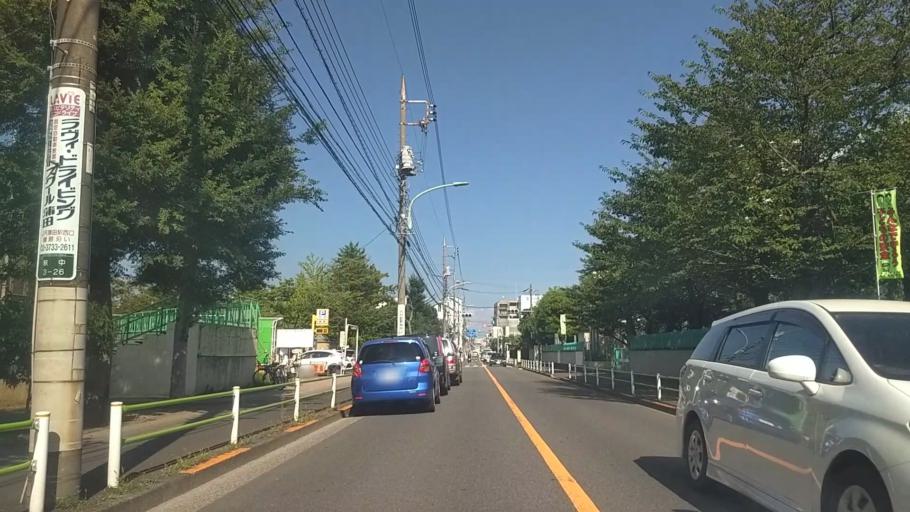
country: JP
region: Kanagawa
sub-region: Kawasaki-shi
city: Kawasaki
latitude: 35.5492
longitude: 139.7382
